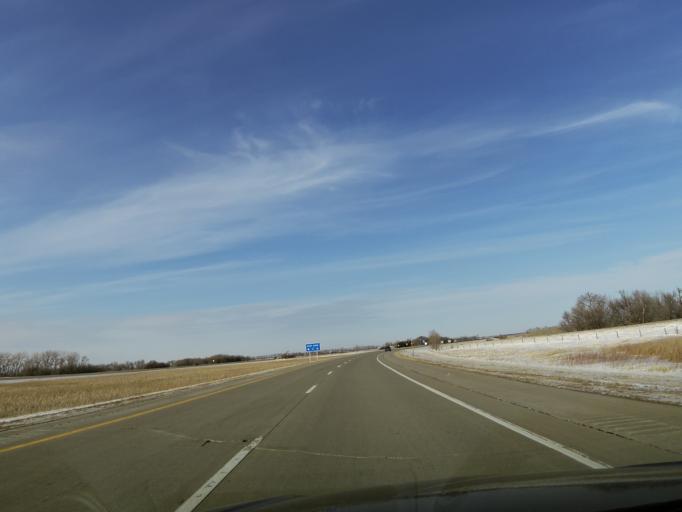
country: US
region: North Dakota
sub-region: Walsh County
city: Grafton
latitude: 48.4524
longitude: -97.1946
